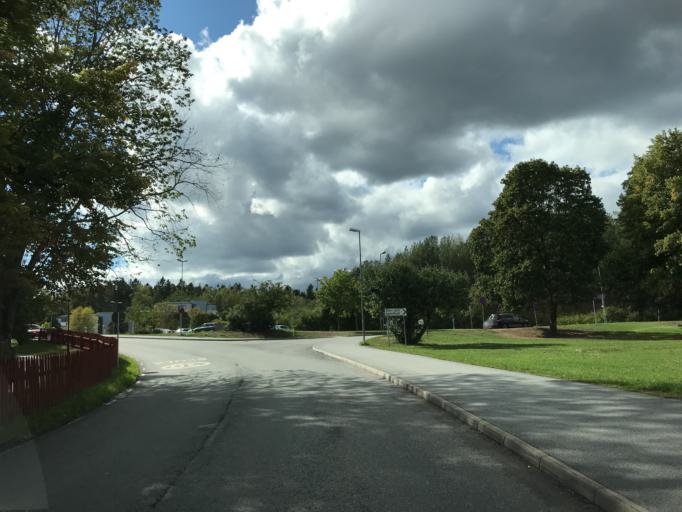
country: SE
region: Stockholm
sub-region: Sollentuna Kommun
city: Sollentuna
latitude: 59.4423
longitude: 17.9529
